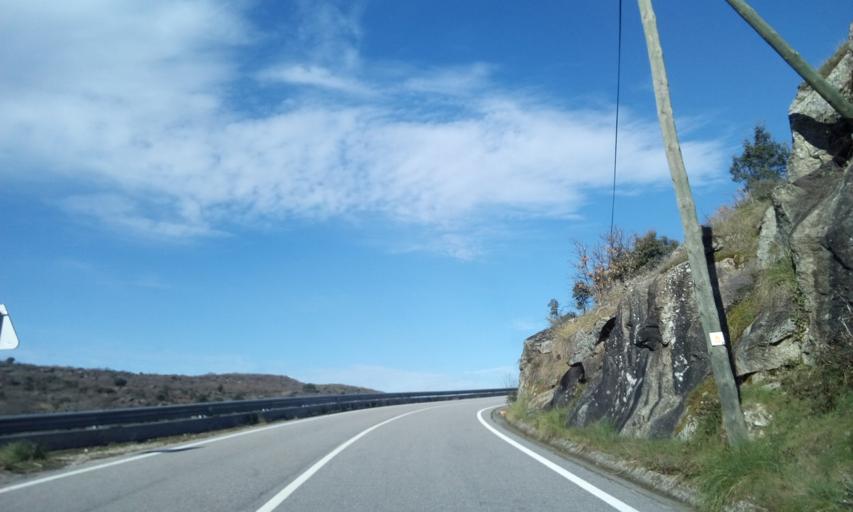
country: ES
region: Castille and Leon
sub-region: Provincia de Salamanca
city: Fuentes de Onoro
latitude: 40.6162
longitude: -6.9169
